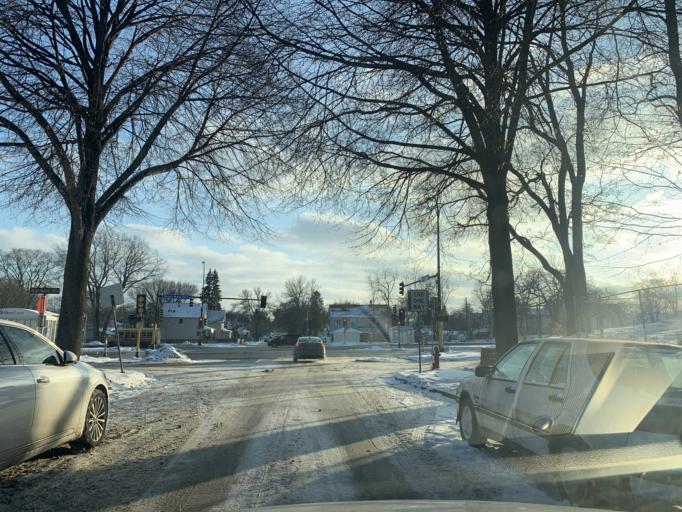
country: US
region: Minnesota
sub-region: Hennepin County
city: Minneapolis
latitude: 44.9850
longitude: -93.3045
